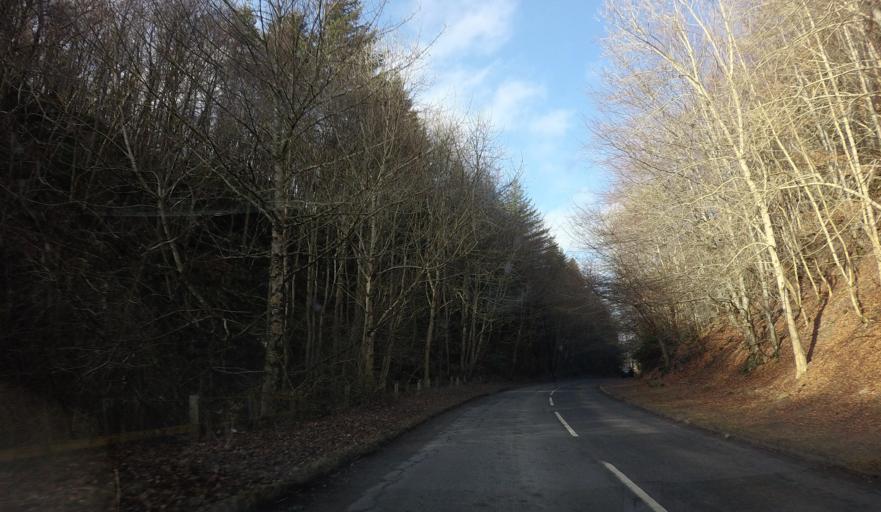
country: GB
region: Scotland
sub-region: Perth and Kinross
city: Bankfoot
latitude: 56.5690
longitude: -3.6124
